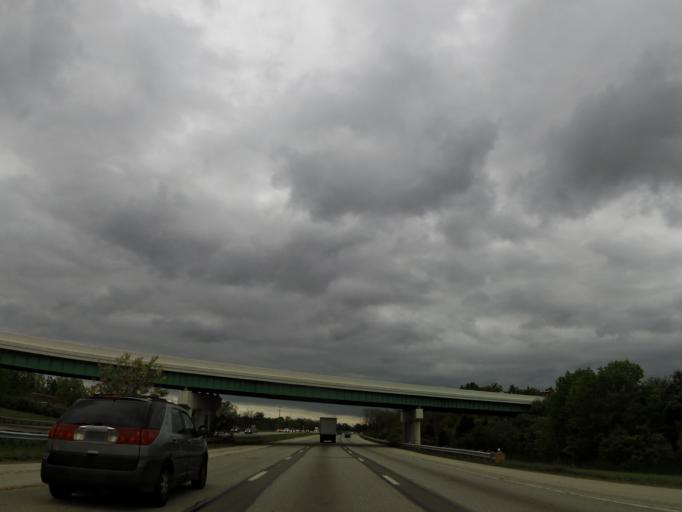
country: US
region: Ohio
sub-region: Warren County
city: Landen
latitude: 39.3336
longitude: -84.2832
